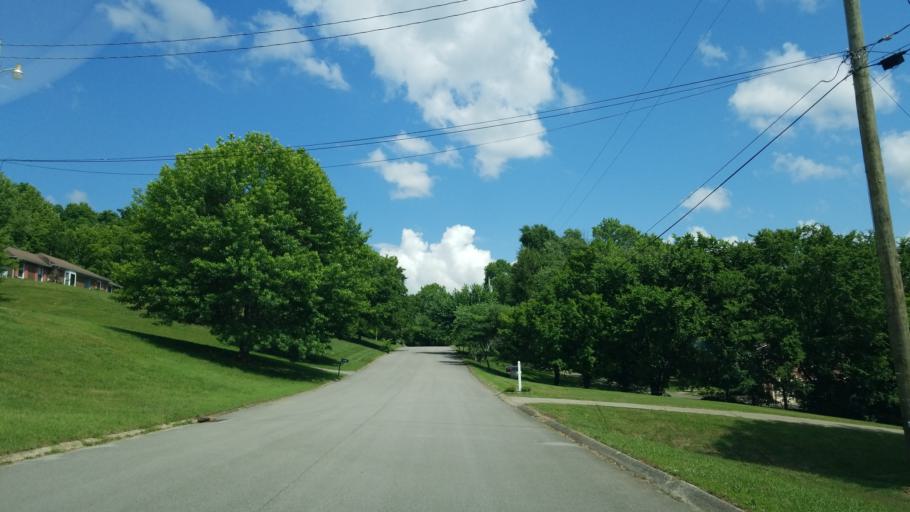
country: US
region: Tennessee
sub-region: Davidson County
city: Forest Hills
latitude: 36.0301
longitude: -86.8506
